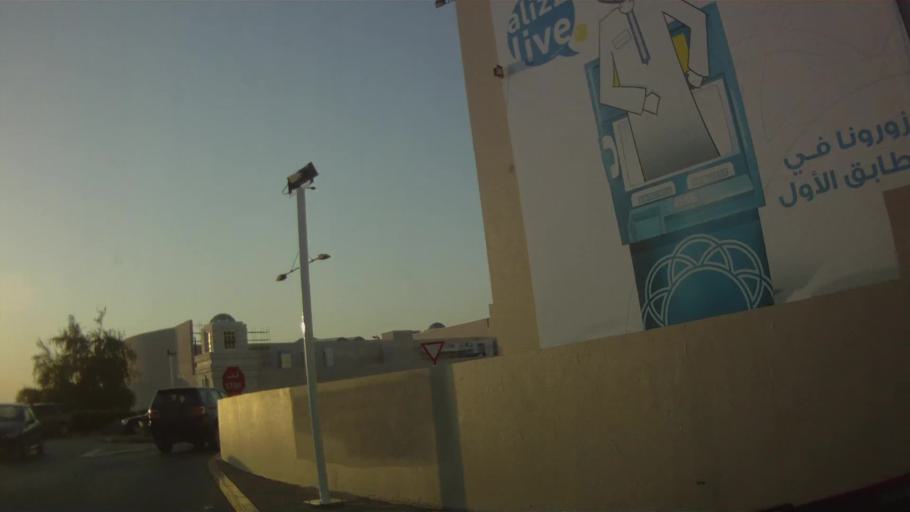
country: OM
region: Muhafazat Masqat
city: Bawshar
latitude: 23.5882
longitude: 58.4122
